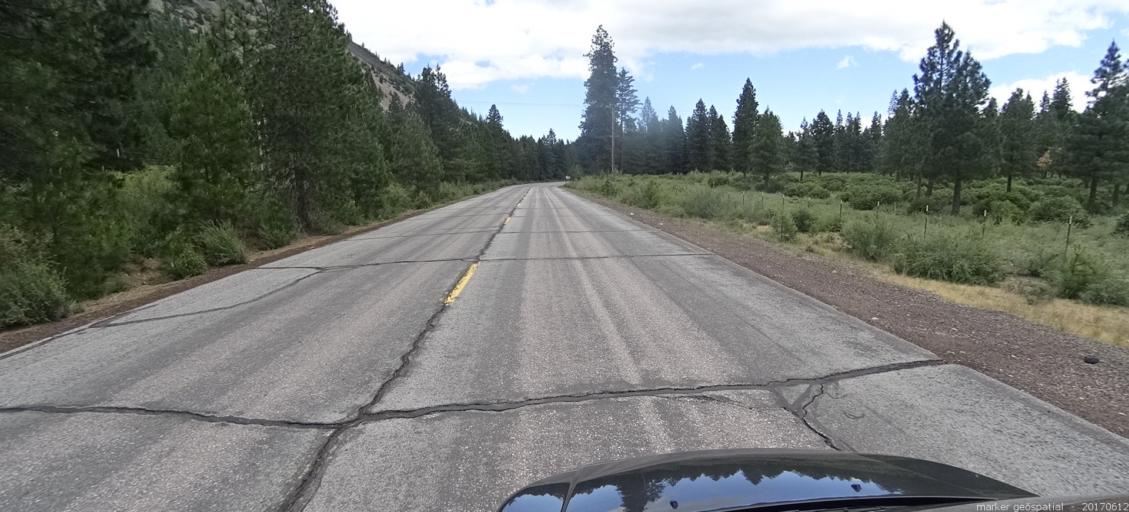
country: US
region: California
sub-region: Siskiyou County
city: Weed
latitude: 41.3654
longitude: -122.3694
